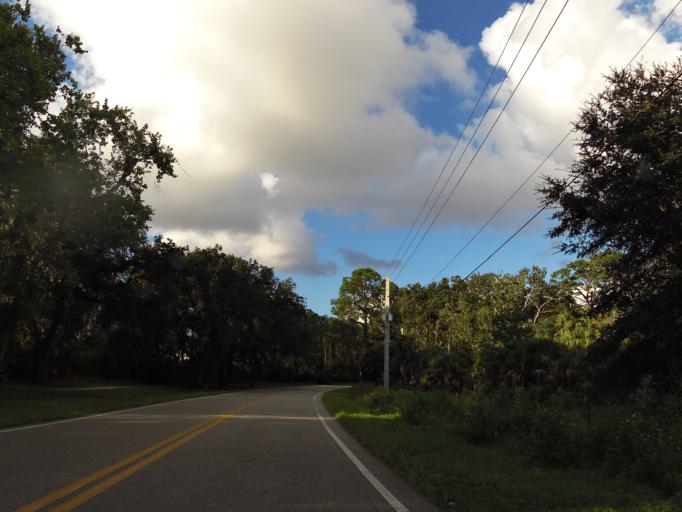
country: US
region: Florida
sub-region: Saint Johns County
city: Palm Valley
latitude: 30.1542
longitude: -81.3746
